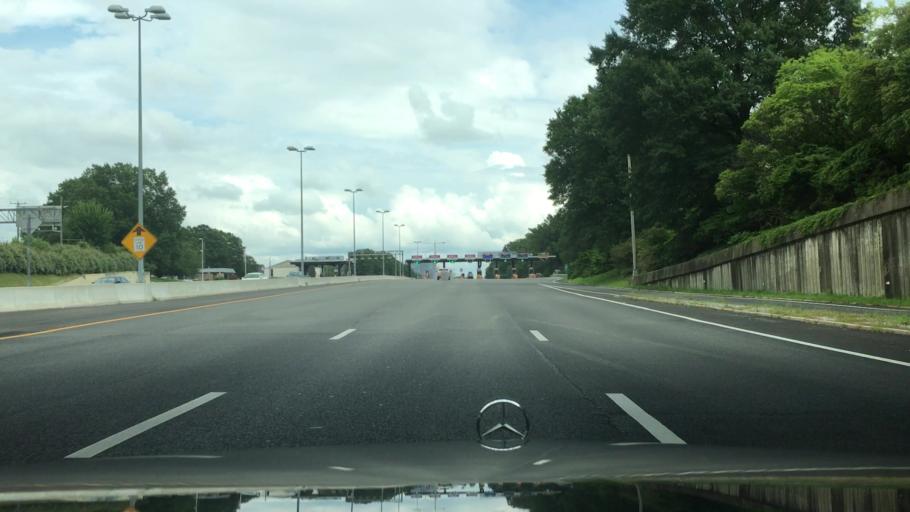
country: US
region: Virginia
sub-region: City of Richmond
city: Richmond
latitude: 37.5459
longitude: -77.4645
